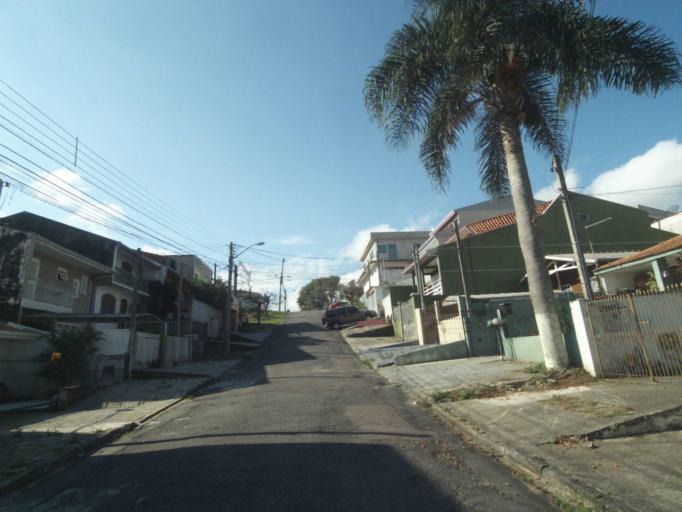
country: BR
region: Parana
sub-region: Curitiba
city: Curitiba
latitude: -25.3954
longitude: -49.3039
